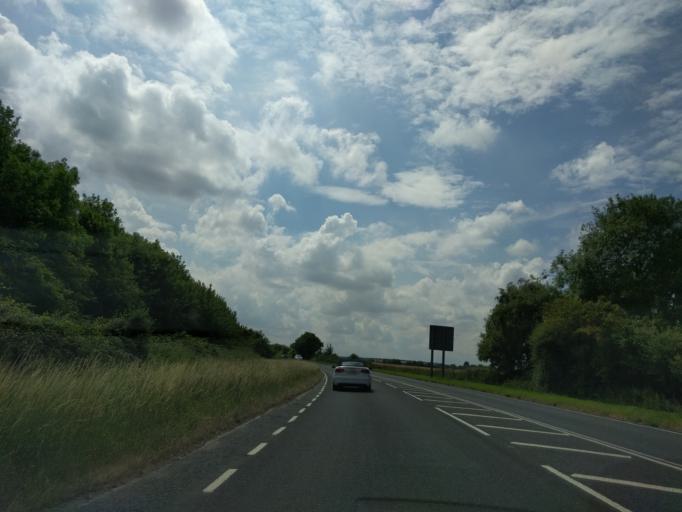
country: GB
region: England
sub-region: Cambridgeshire
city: Fulbourn
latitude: 52.2042
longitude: 0.1852
